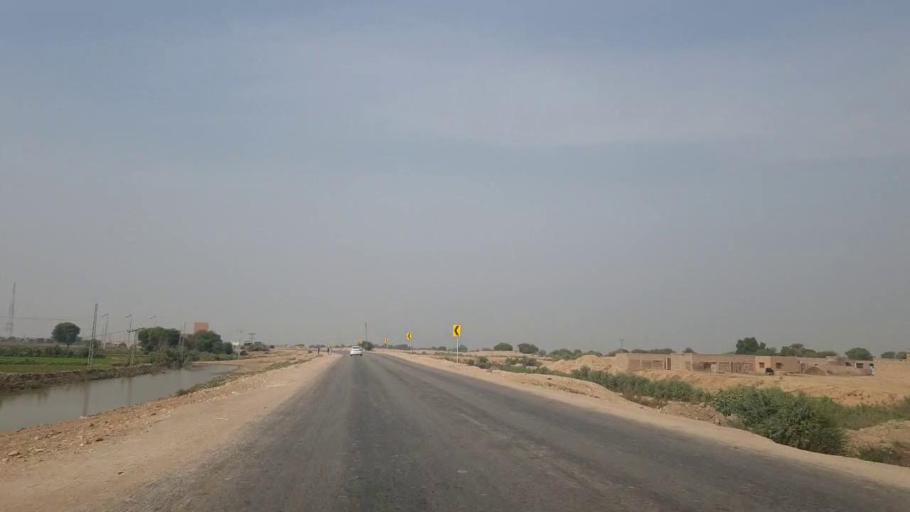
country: PK
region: Sindh
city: Sann
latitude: 26.0900
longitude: 68.0903
